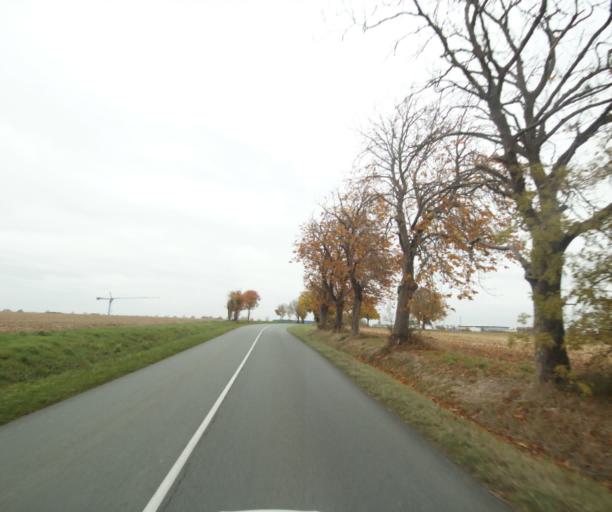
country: FR
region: Poitou-Charentes
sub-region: Departement de la Charente-Maritime
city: Les Gonds
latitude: 45.7137
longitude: -0.6447
